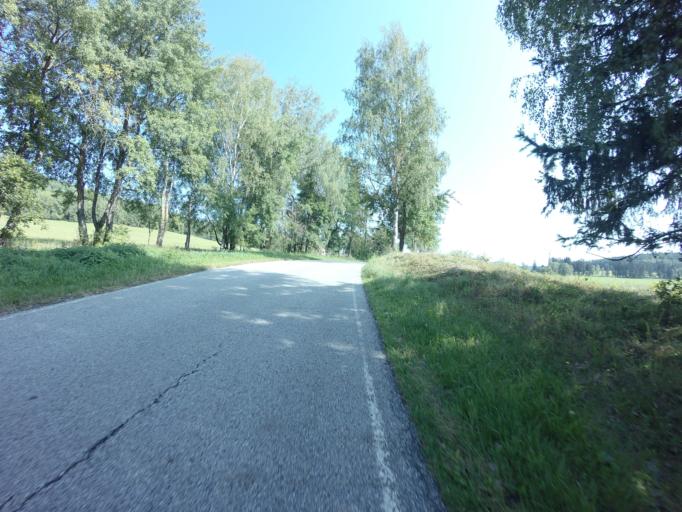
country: CZ
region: Jihocesky
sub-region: Okres Cesky Krumlov
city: Vyssi Brod
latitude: 48.6298
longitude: 14.3394
